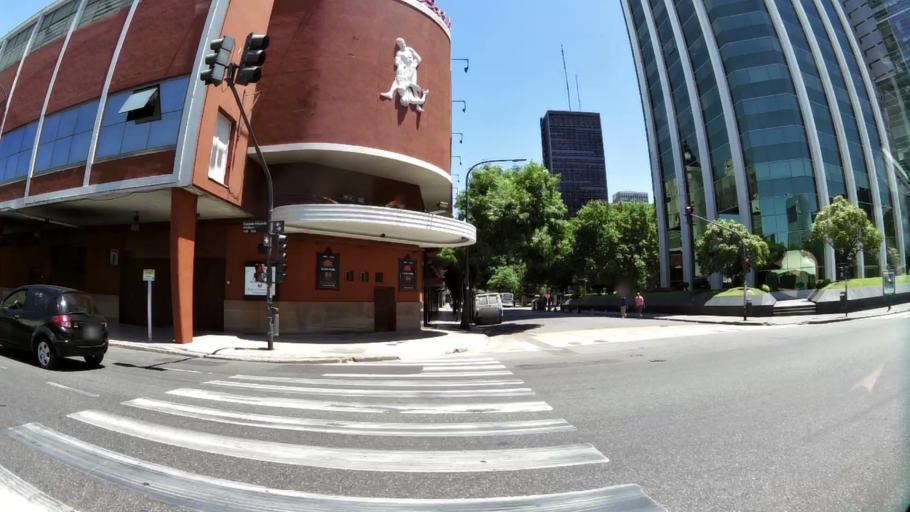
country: AR
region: Buenos Aires F.D.
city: Buenos Aires
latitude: -34.6018
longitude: -58.3683
